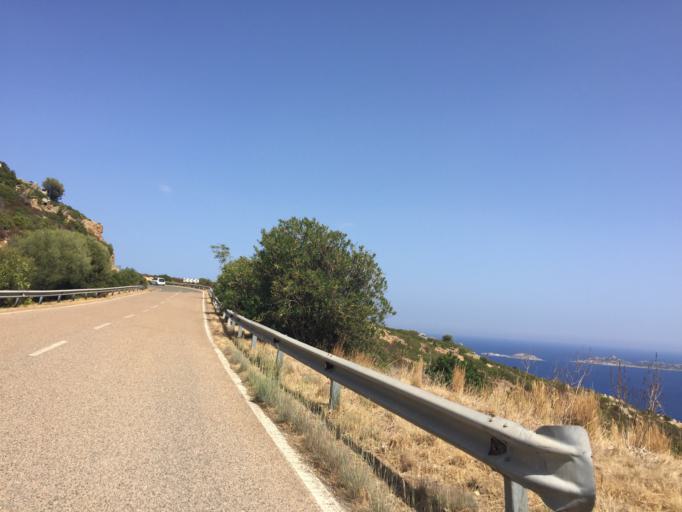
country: IT
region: Sardinia
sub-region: Provincia di Cagliari
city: Villasimius
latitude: 39.1519
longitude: 9.5588
